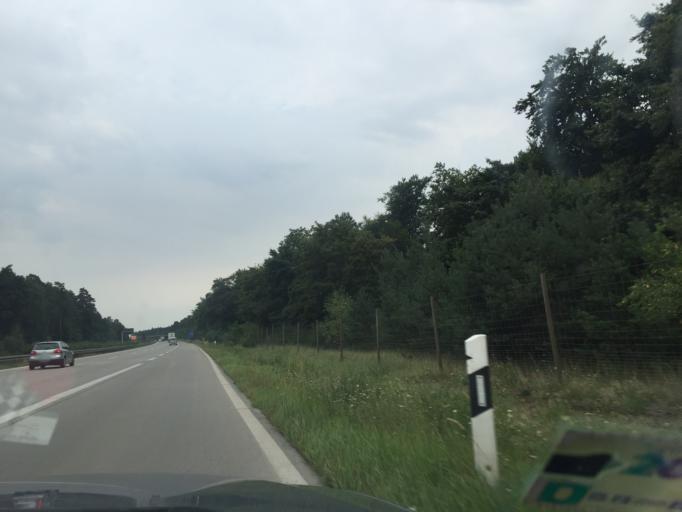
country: DE
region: Brandenburg
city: Bernau bei Berlin
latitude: 52.7265
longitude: 13.5405
